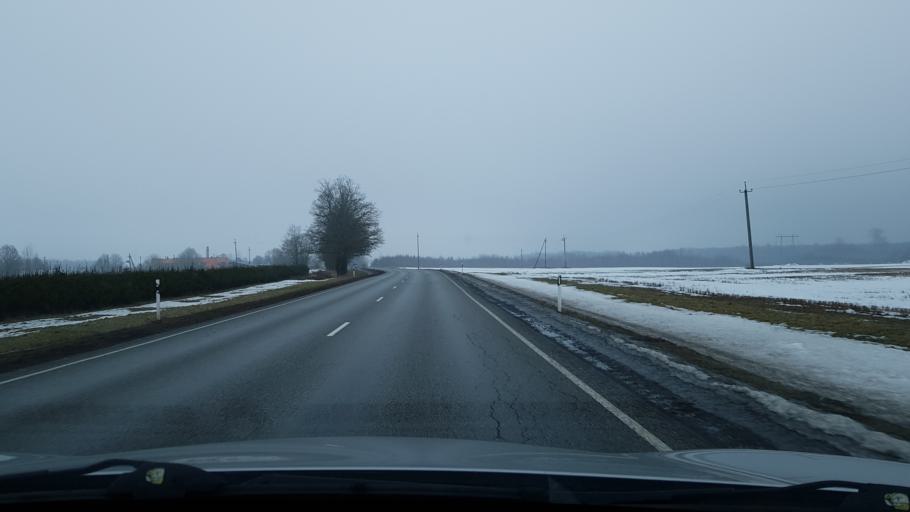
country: EE
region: Valgamaa
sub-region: Valga linn
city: Valga
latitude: 57.9353
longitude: 26.1706
